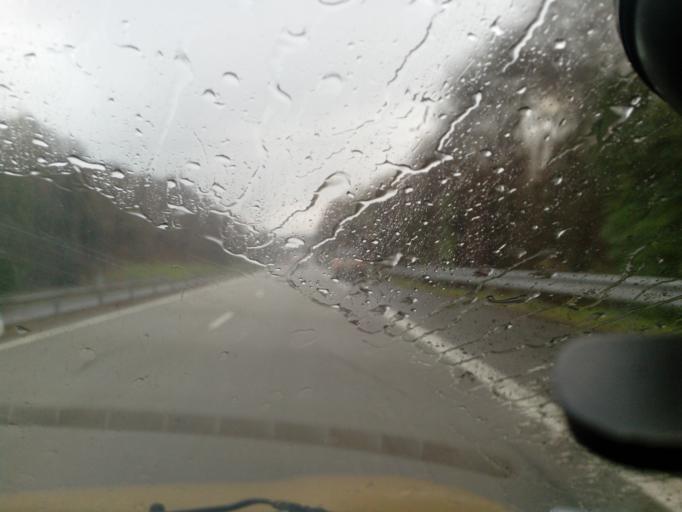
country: FR
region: Brittany
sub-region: Departement du Morbihan
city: Baud
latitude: 47.8782
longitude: -3.0503
